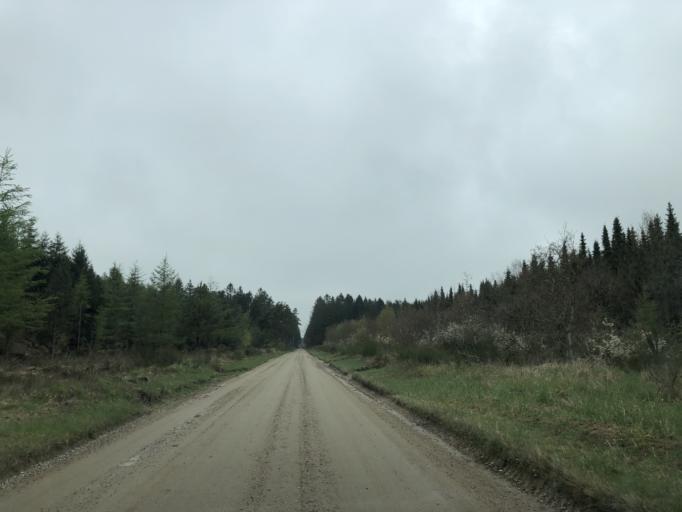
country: DK
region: Central Jutland
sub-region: Lemvig Kommune
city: Lemvig
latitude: 56.4970
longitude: 8.3393
